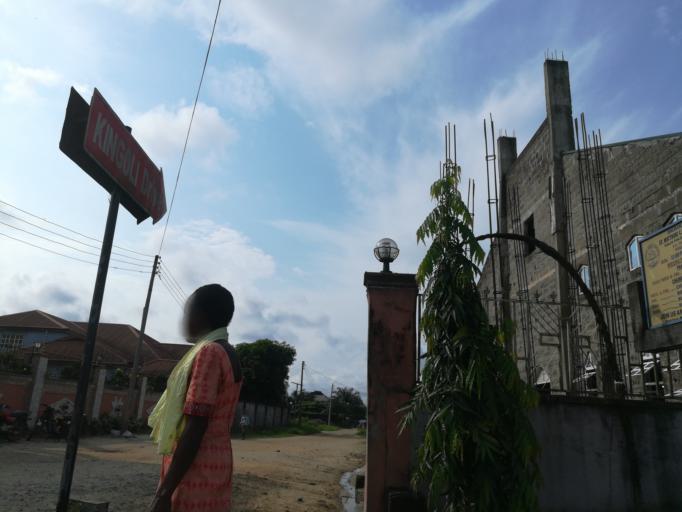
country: NG
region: Rivers
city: Okrika
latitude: 4.7467
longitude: 7.0846
